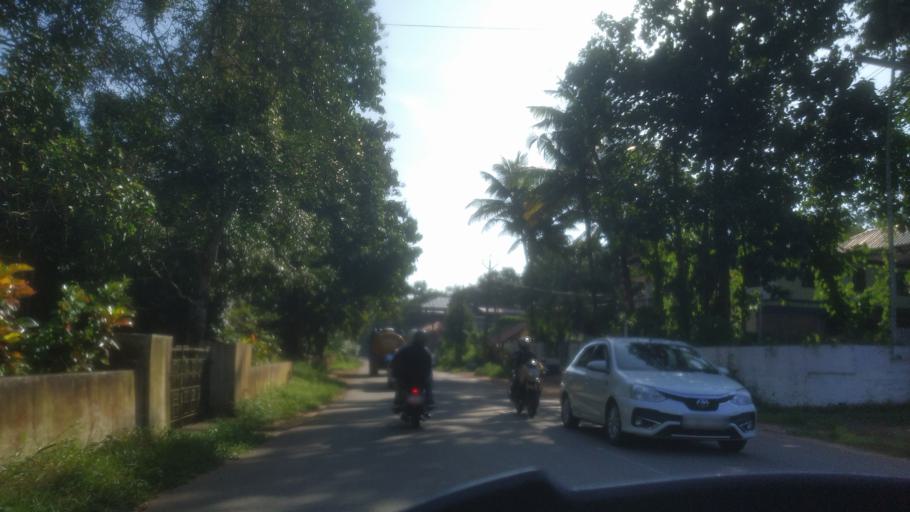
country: IN
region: Kerala
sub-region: Ernakulam
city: Ramamangalam
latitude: 9.9790
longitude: 76.5151
